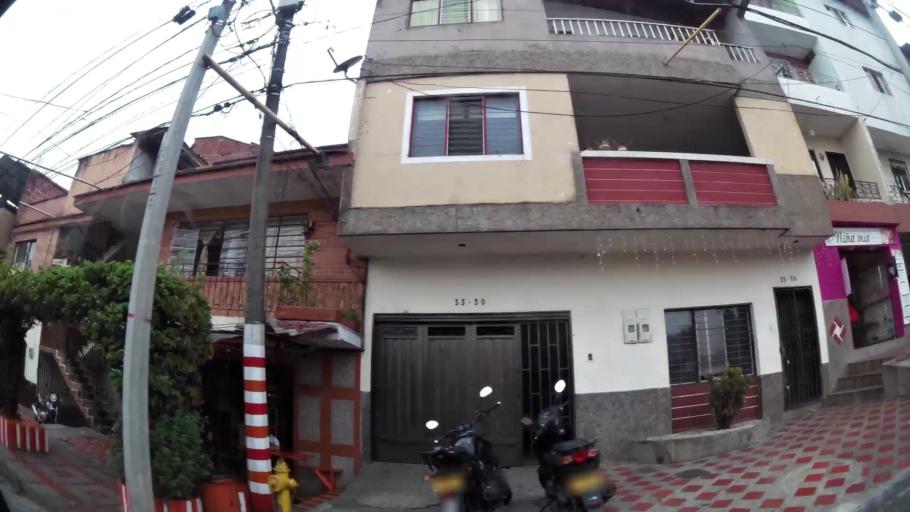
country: CO
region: Antioquia
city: Medellin
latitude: 6.2450
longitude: -75.5534
